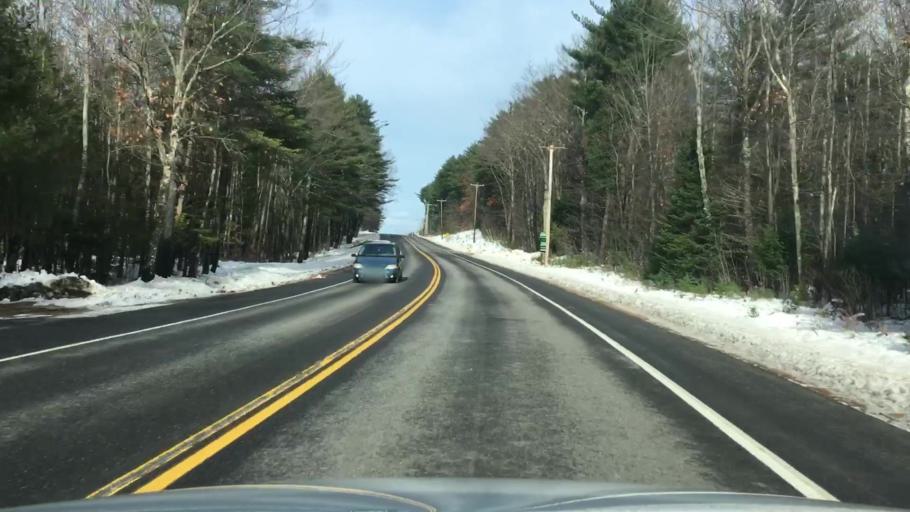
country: US
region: Maine
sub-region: Androscoggin County
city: Greene
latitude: 44.2064
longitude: -70.0998
